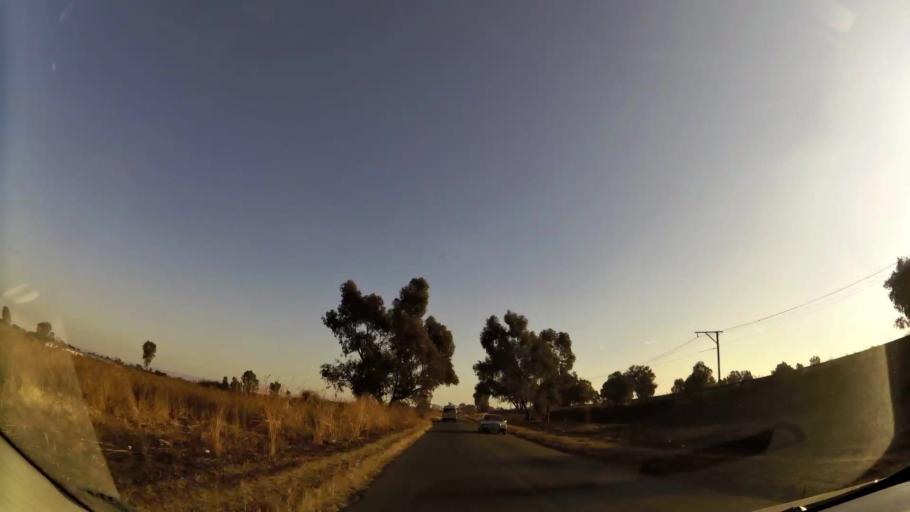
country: ZA
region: Gauteng
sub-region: West Rand District Municipality
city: Randfontein
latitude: -26.1970
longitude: 27.6779
